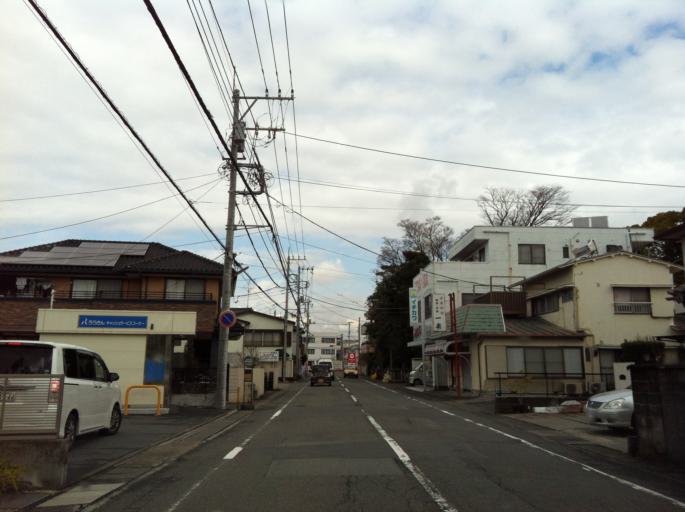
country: JP
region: Shizuoka
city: Fuji
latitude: 35.1477
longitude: 138.6580
